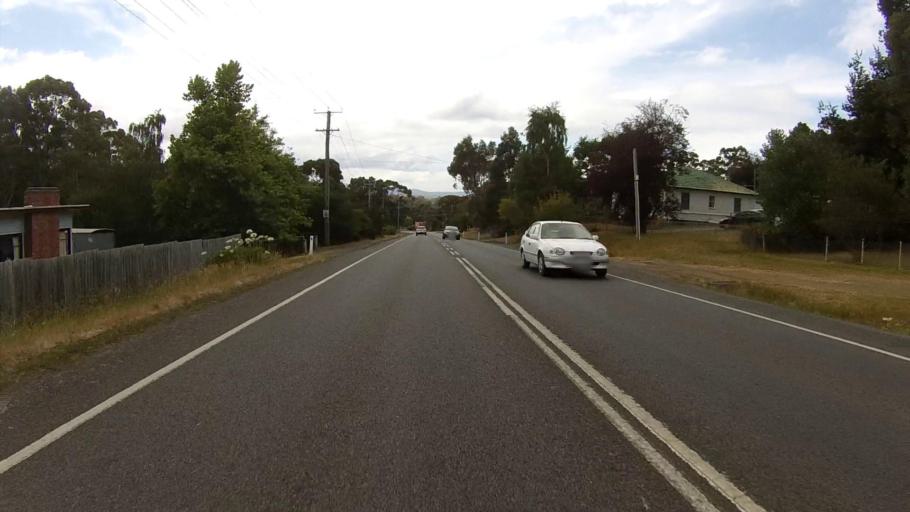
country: AU
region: Tasmania
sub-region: Kingborough
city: Kettering
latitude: -43.0784
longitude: 147.2559
